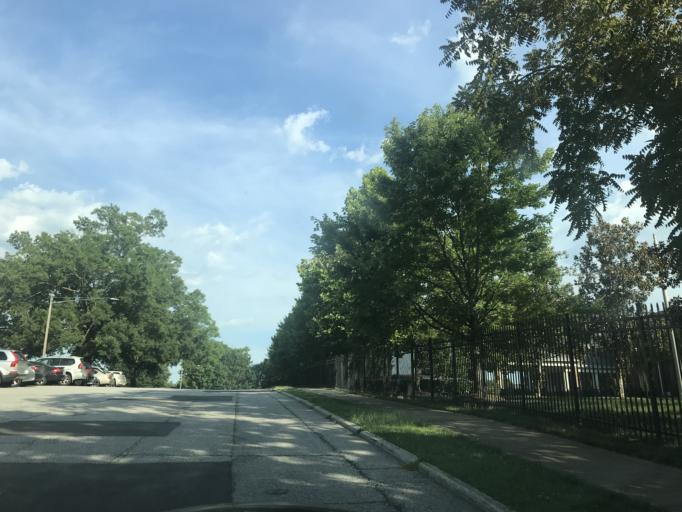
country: US
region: North Carolina
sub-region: Wake County
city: Raleigh
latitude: 35.7721
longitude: -78.6278
